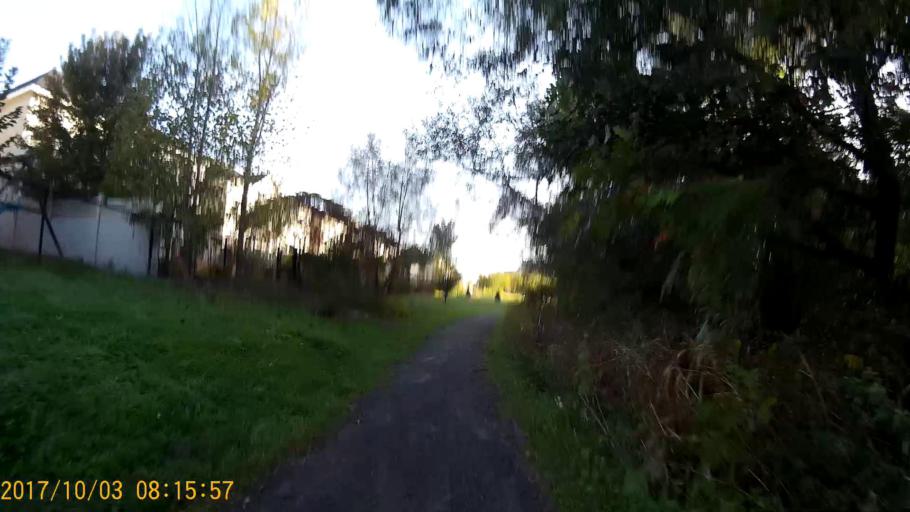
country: CA
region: Ontario
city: Bells Corners
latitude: 45.3592
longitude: -75.9337
